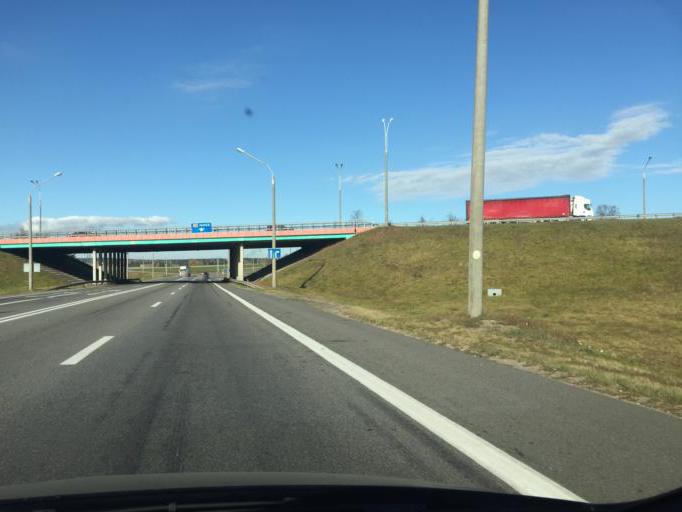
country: BY
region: Minsk
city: Slabada
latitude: 54.0149
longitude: 27.8919
